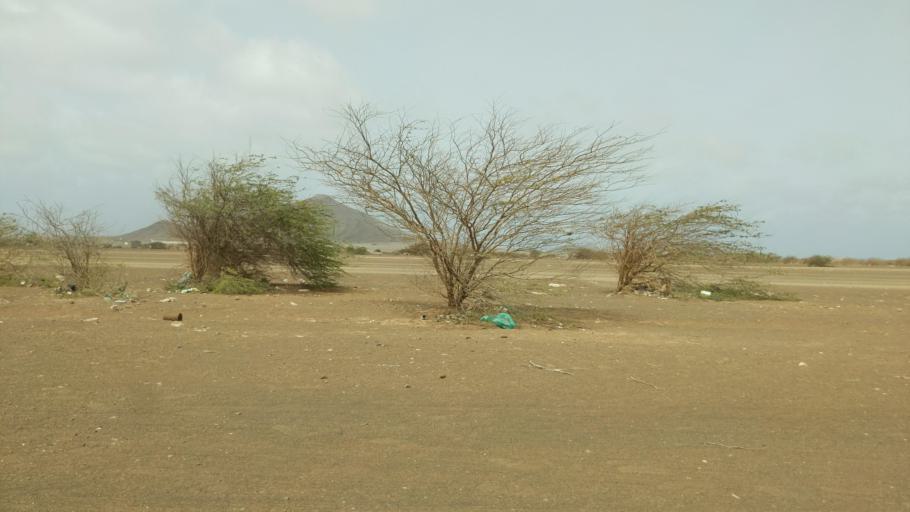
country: CV
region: Sal
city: Espargos
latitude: 16.7698
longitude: -22.9459
